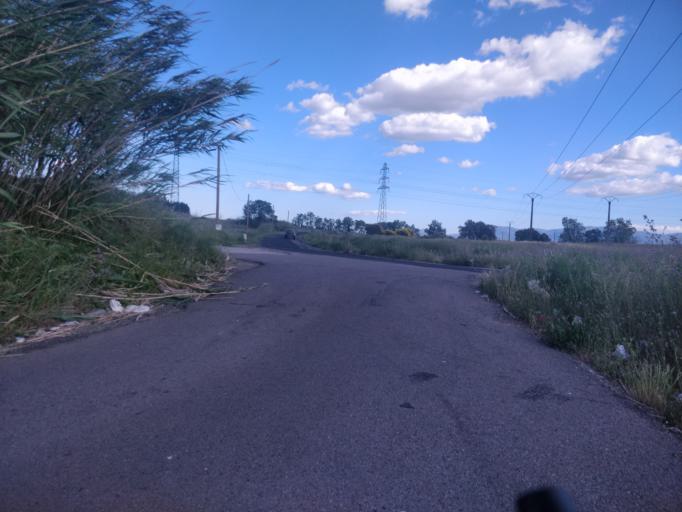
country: FR
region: Languedoc-Roussillon
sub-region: Departement des Pyrenees-Orientales
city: Cabestany
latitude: 42.6798
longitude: 2.9194
